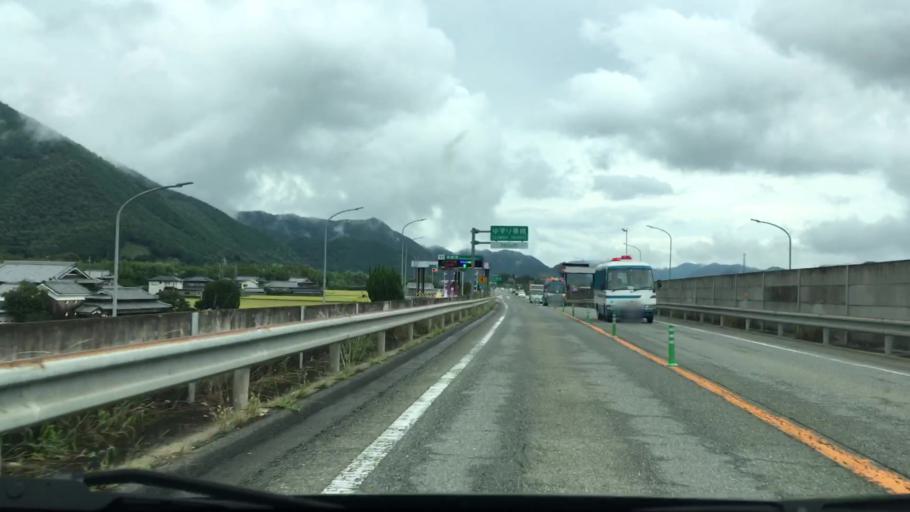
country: JP
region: Hyogo
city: Yamazakicho-nakabirose
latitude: 35.0569
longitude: 134.7637
